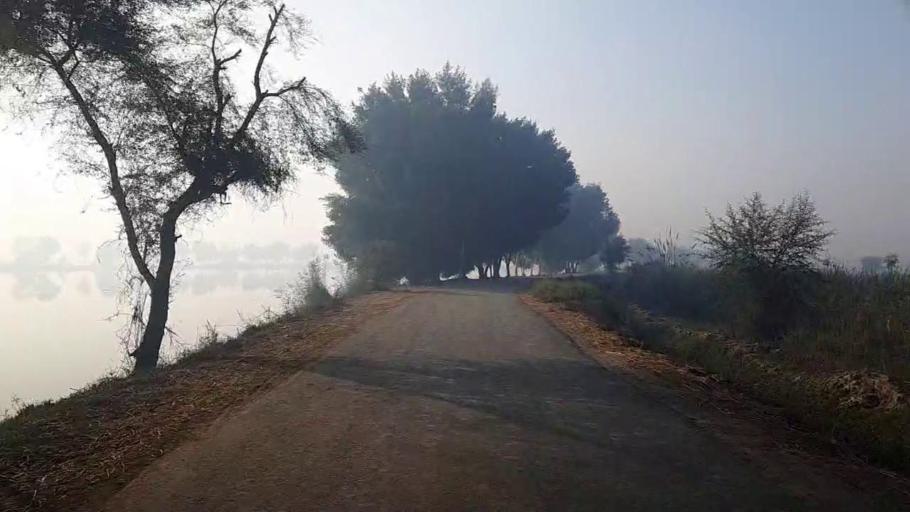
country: PK
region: Sindh
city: Mehar
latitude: 27.1502
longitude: 67.8238
